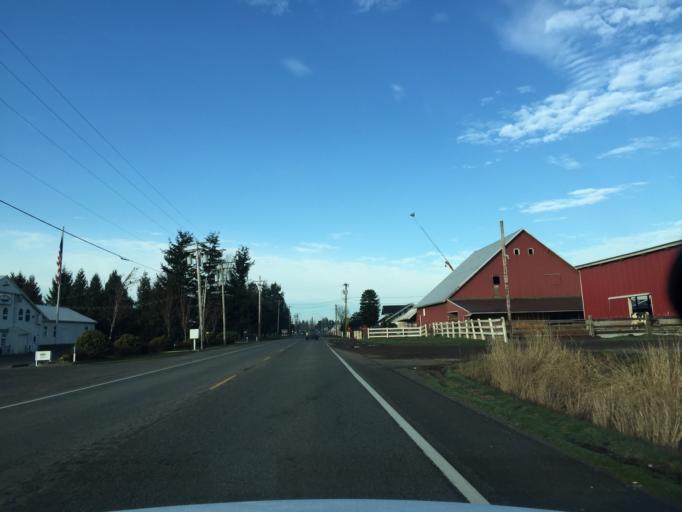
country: US
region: Washington
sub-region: Whatcom County
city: Lynden
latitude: 48.9645
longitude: -122.4450
